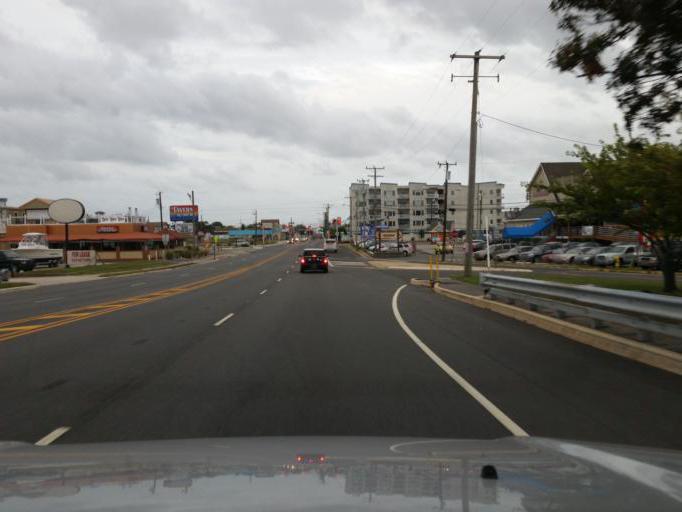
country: US
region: New Jersey
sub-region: Cape May County
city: Wildwood Crest
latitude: 38.9896
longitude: -74.8314
